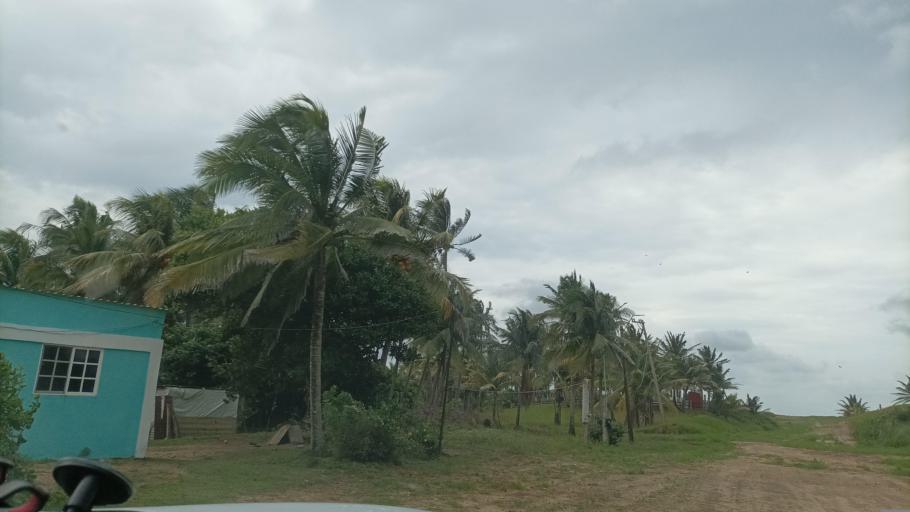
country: MX
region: Veracruz
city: Agua Dulce
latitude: 18.2075
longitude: -94.1476
